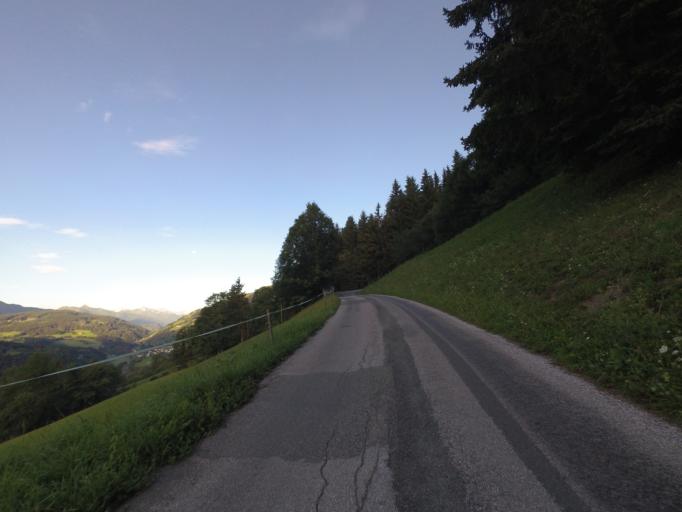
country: AT
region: Salzburg
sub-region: Politischer Bezirk Sankt Johann im Pongau
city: Goldegg
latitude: 47.3380
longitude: 13.1036
